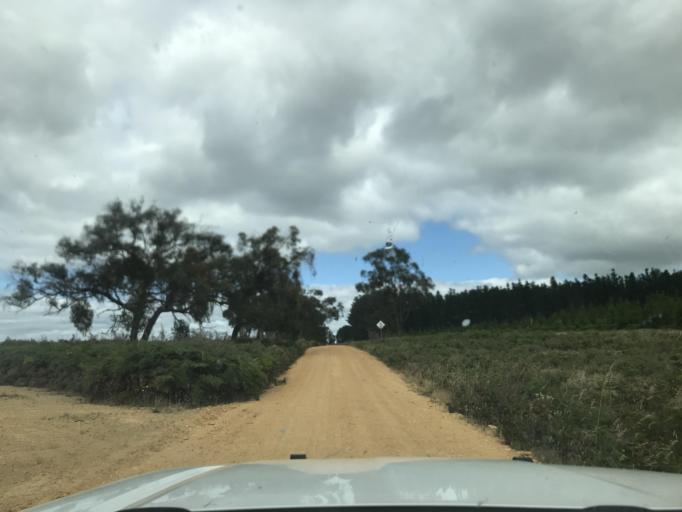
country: AU
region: South Australia
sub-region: Wattle Range
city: Penola
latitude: -37.3171
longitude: 141.1582
